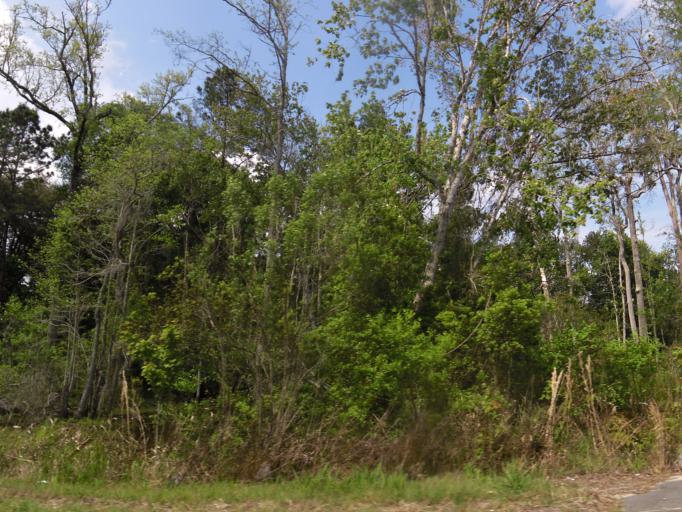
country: US
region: Georgia
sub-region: Camden County
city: Kingsland
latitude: 30.8103
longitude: -81.7776
